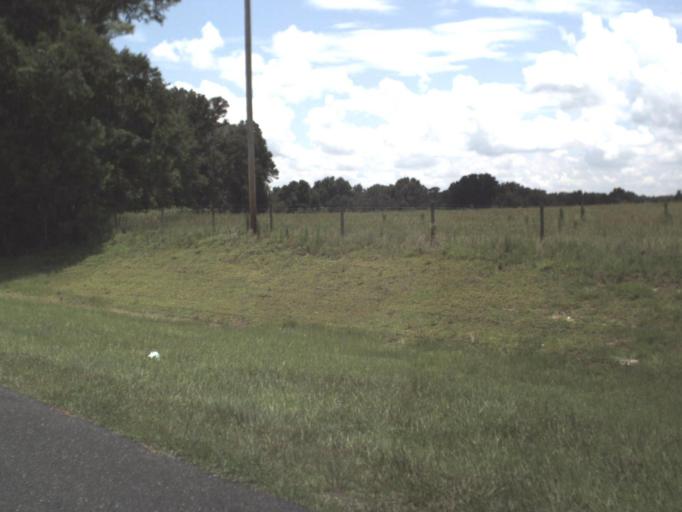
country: US
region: Florida
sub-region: Levy County
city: Williston
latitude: 29.3808
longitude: -82.4228
